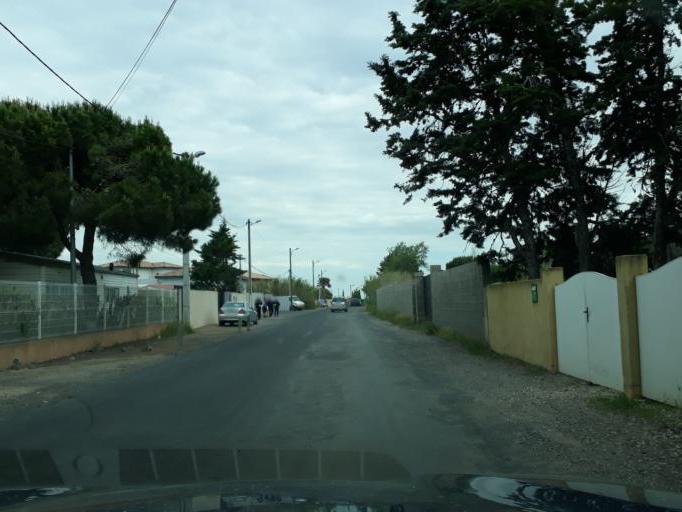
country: FR
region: Languedoc-Roussillon
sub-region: Departement de l'Herault
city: Agde
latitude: 43.2855
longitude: 3.4750
